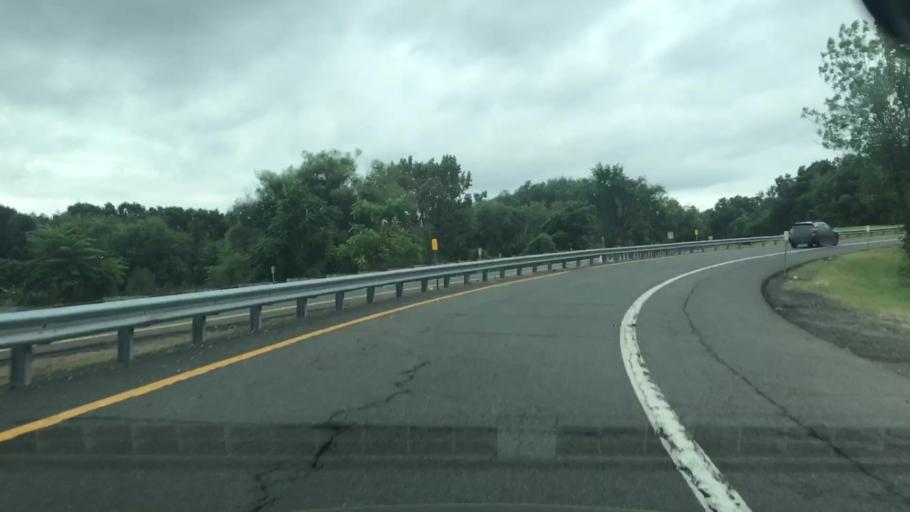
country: US
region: New York
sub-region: Rockland County
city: Bardonia
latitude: 41.1004
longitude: -73.9895
